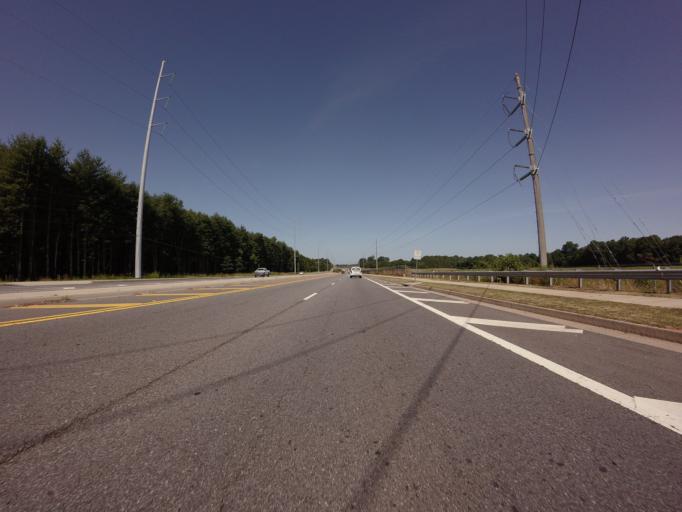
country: US
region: Georgia
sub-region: Gwinnett County
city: Suwanee
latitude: 34.0508
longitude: -84.1007
